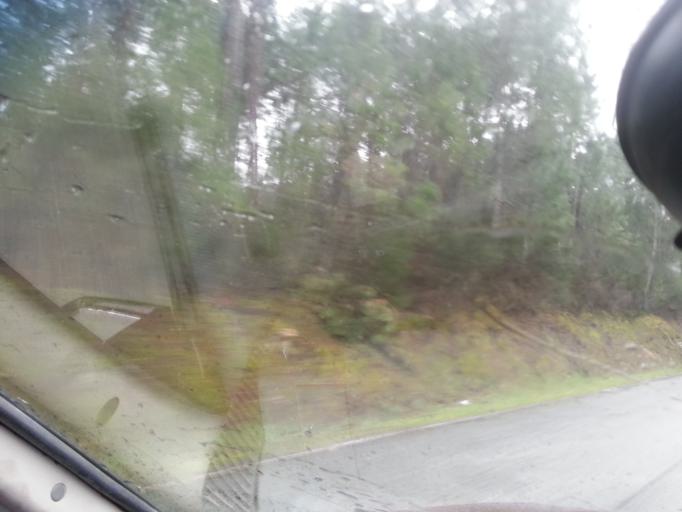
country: PT
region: Guarda
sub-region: Fornos de Algodres
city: Fornos de Algodres
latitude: 40.6103
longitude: -7.6255
